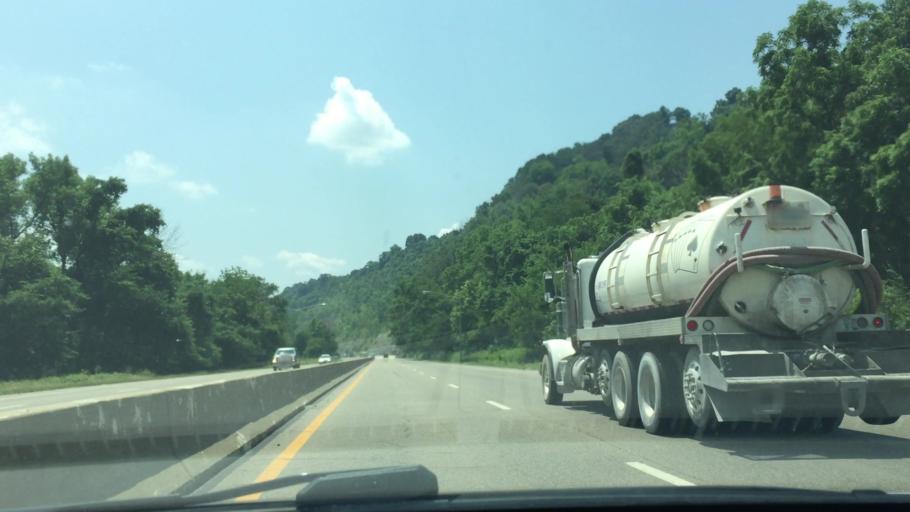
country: US
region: West Virginia
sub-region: Marshall County
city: Glendale
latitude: 39.9569
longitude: -80.7628
